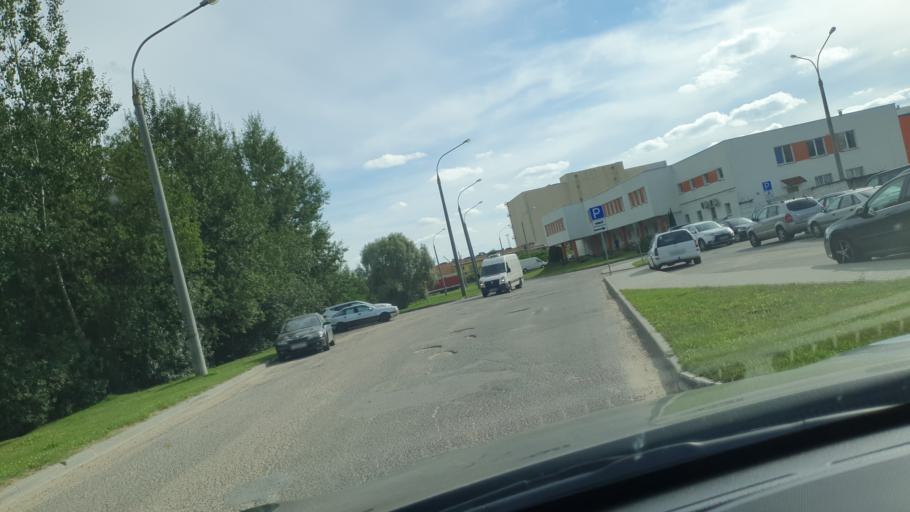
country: BY
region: Minsk
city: Azyartso
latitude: 53.8631
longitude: 27.3999
